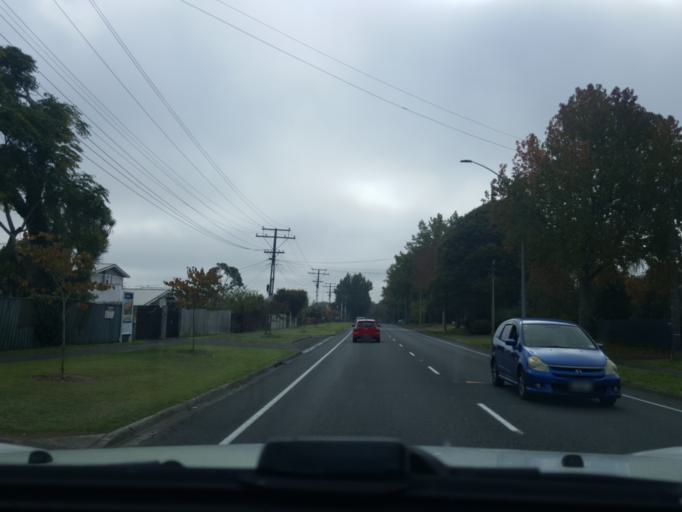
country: NZ
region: Waikato
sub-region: Hamilton City
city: Hamilton
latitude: -37.7551
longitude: 175.2829
